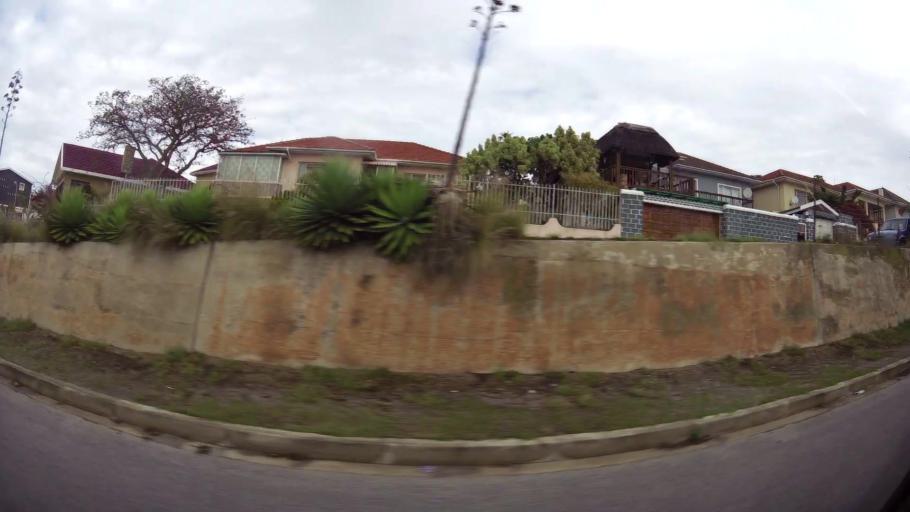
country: ZA
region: Eastern Cape
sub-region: Nelson Mandela Bay Metropolitan Municipality
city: Port Elizabeth
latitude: -33.9449
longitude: 25.5947
